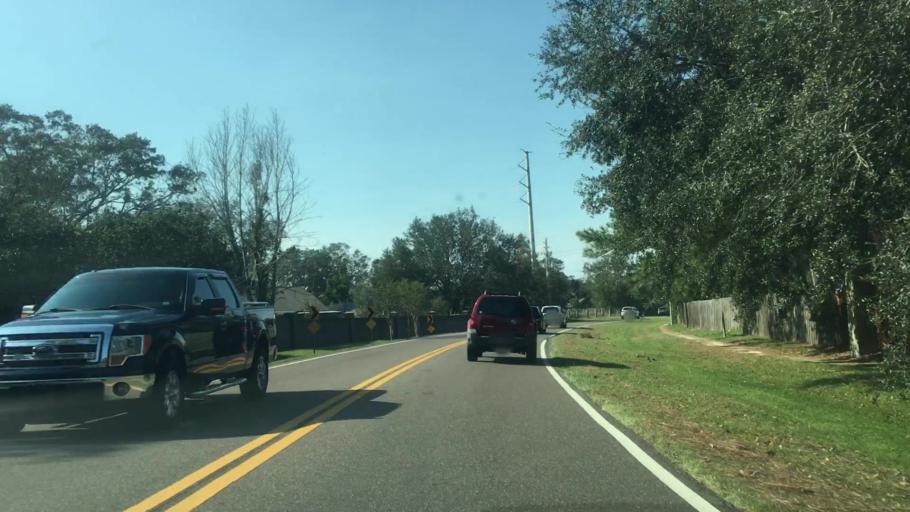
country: US
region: Florida
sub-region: Duval County
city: Neptune Beach
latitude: 30.3022
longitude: -81.4433
